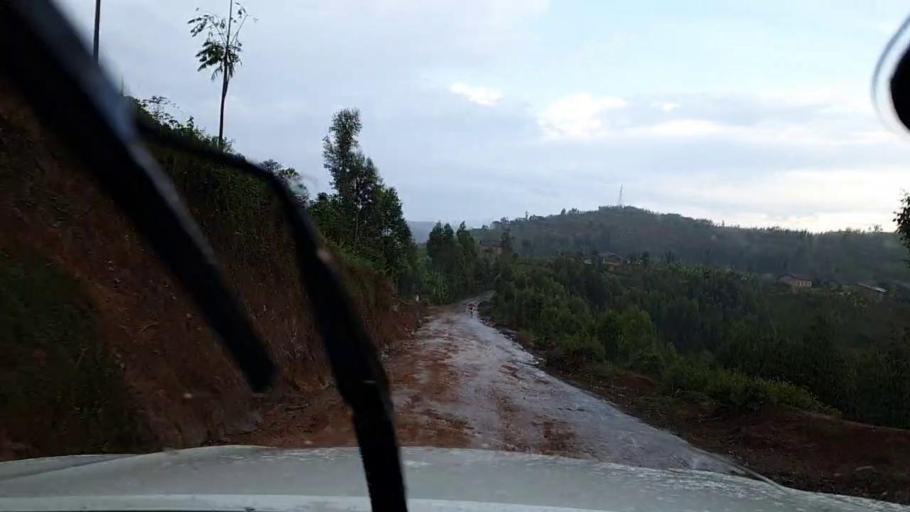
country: BI
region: Kayanza
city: Kayanza
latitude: -2.7740
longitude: 29.5443
